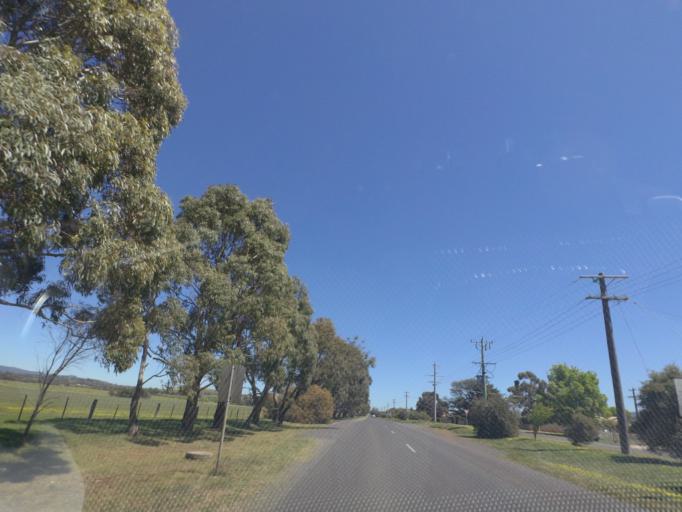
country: AU
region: Victoria
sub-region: Hume
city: Sunbury
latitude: -37.2792
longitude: 144.7216
